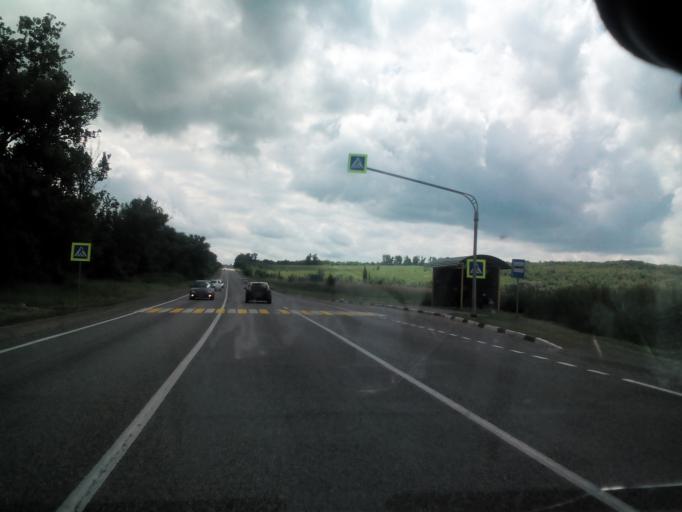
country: RU
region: Stavropol'skiy
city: Stavropol'
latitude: 44.9933
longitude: 42.0067
